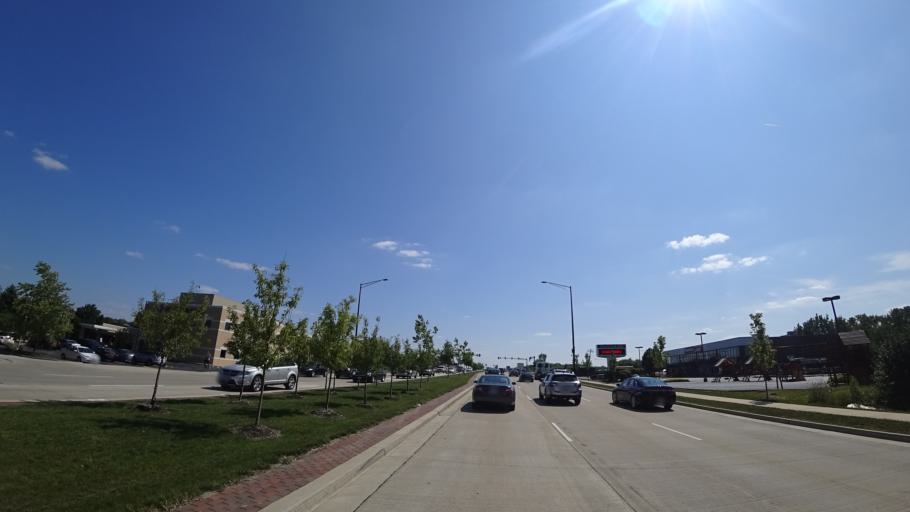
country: US
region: Illinois
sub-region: Cook County
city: Orland Hills
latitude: 41.5885
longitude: -87.8524
